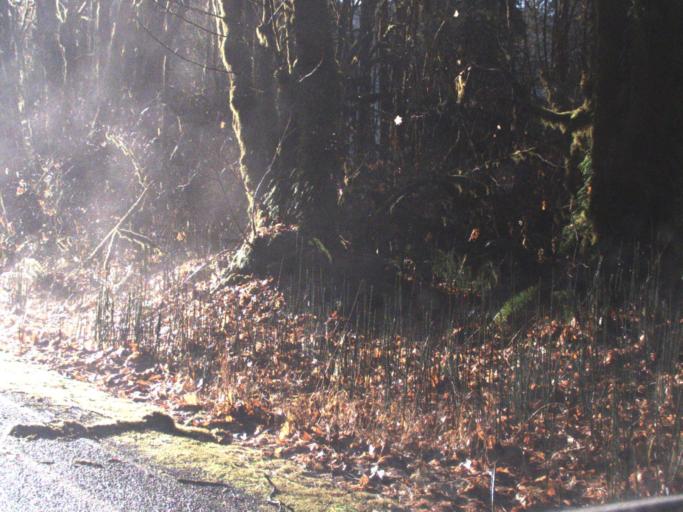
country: US
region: Washington
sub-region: Snohomish County
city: Darrington
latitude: 48.4536
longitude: -121.5918
